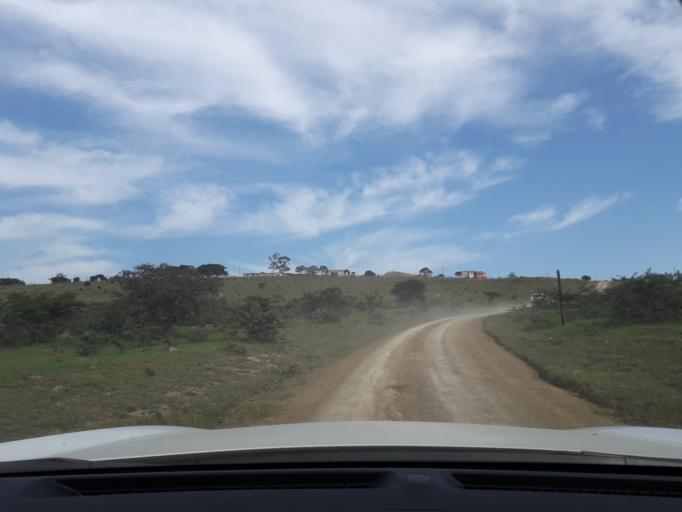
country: ZA
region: Eastern Cape
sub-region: Buffalo City Metropolitan Municipality
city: Bhisho
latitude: -32.9970
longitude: 27.3361
